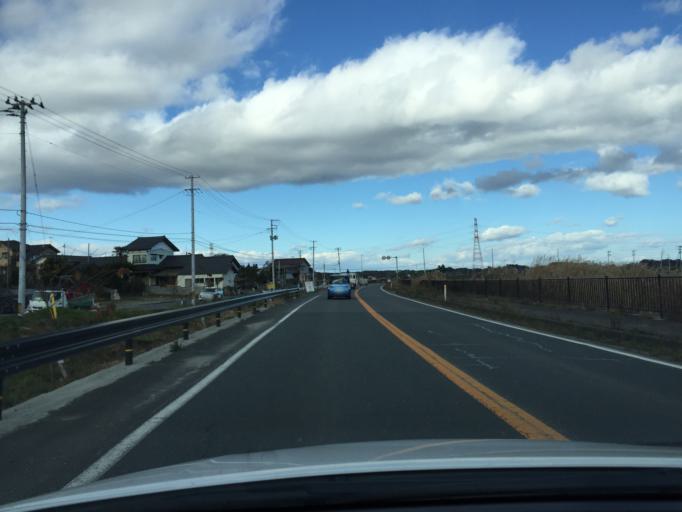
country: JP
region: Fukushima
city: Namie
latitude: 37.5892
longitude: 141.0059
